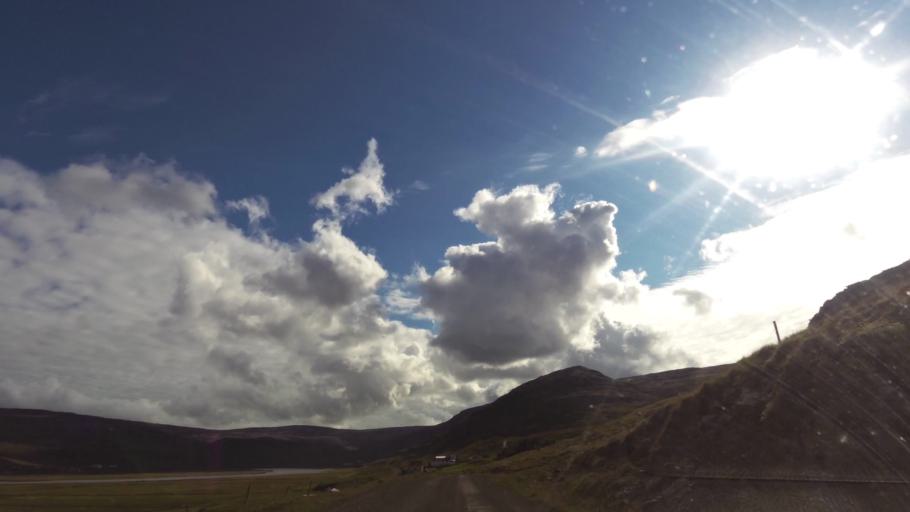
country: IS
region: West
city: Olafsvik
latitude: 65.5793
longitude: -24.1466
